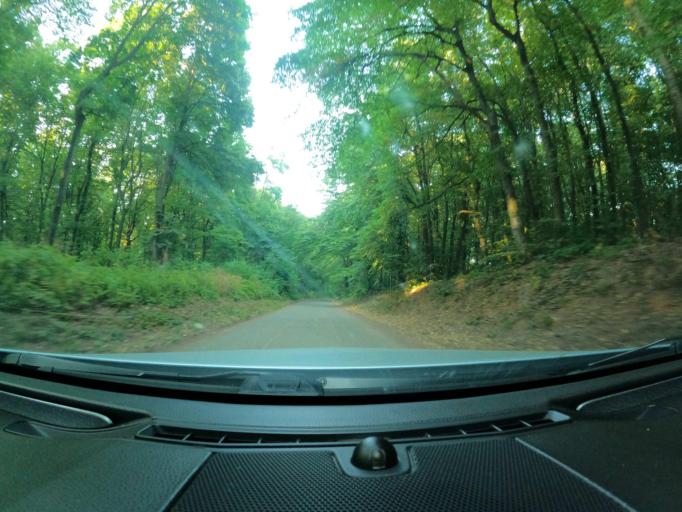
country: RS
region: Autonomna Pokrajina Vojvodina
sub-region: Juznobacki Okrug
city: Beocin
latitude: 45.1539
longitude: 19.7295
